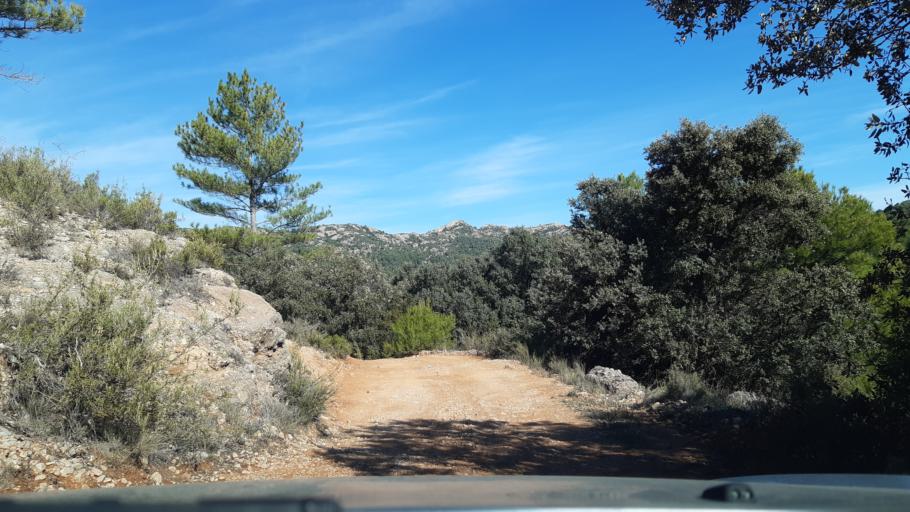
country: ES
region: Aragon
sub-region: Provincia de Teruel
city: Valderrobres
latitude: 40.8401
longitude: 0.2042
